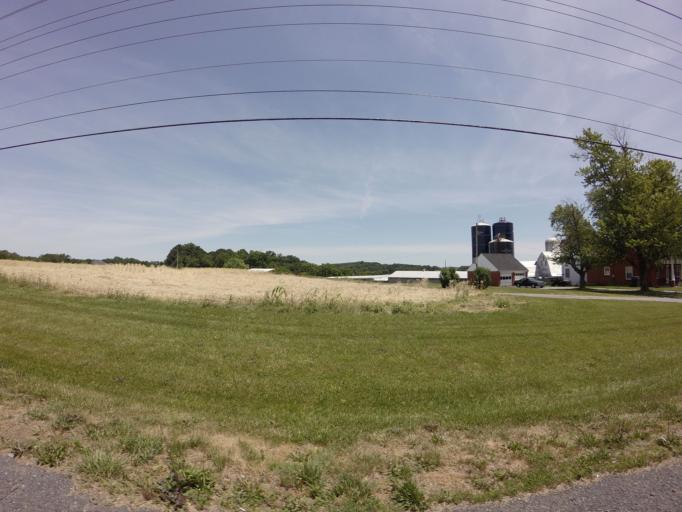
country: US
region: Maryland
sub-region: Frederick County
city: Urbana
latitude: 39.3426
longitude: -77.3737
